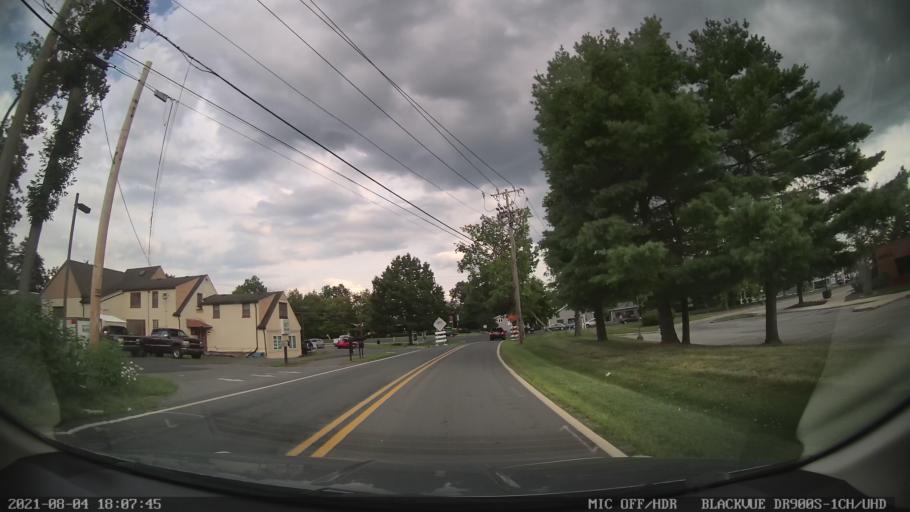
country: US
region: Pennsylvania
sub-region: Lehigh County
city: Ancient Oaks
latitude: 40.5585
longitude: -75.5749
